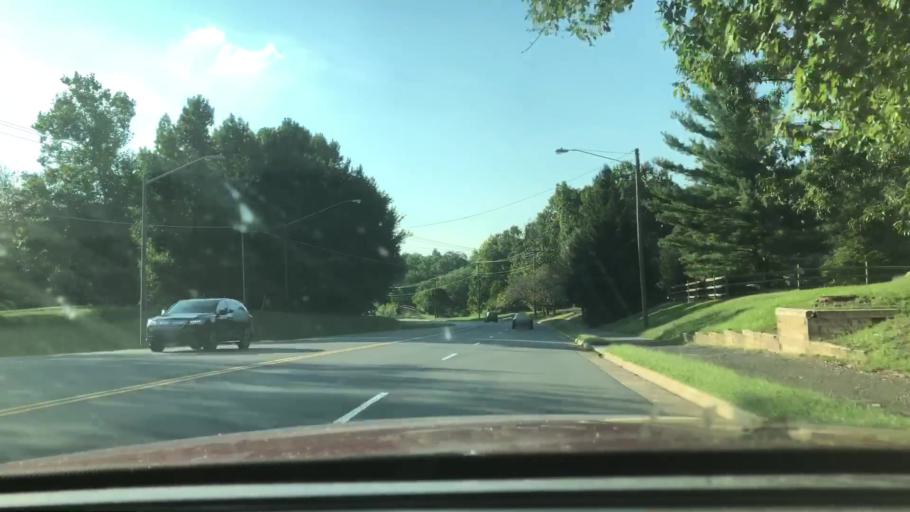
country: US
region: Virginia
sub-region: Fairfax County
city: Centreville
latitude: 38.8331
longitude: -77.4152
